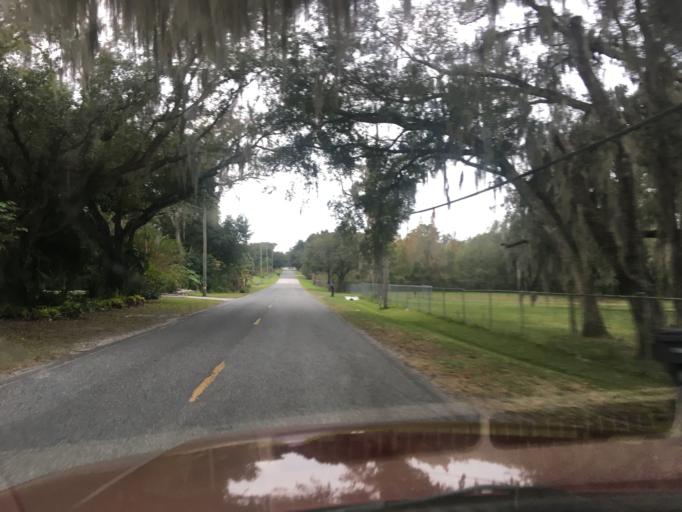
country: US
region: Florida
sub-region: Hillsborough County
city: Plant City
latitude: 28.0422
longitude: -82.0970
